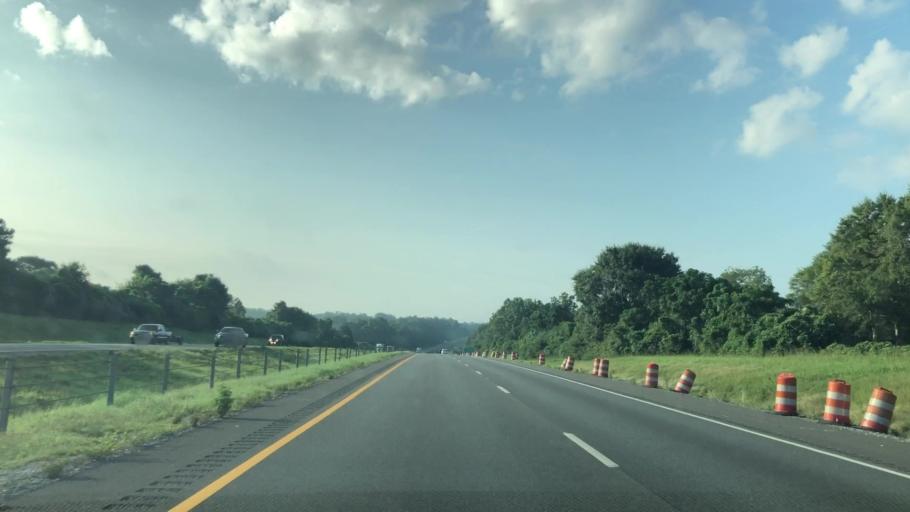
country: US
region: Alabama
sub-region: Chilton County
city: Clanton
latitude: 32.8635
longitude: -86.6062
